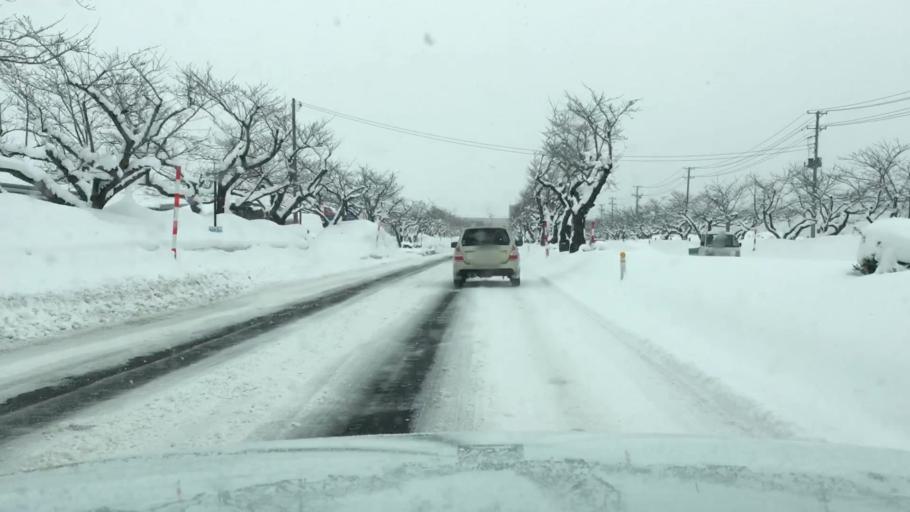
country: JP
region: Aomori
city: Hirosaki
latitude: 40.6371
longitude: 140.4889
